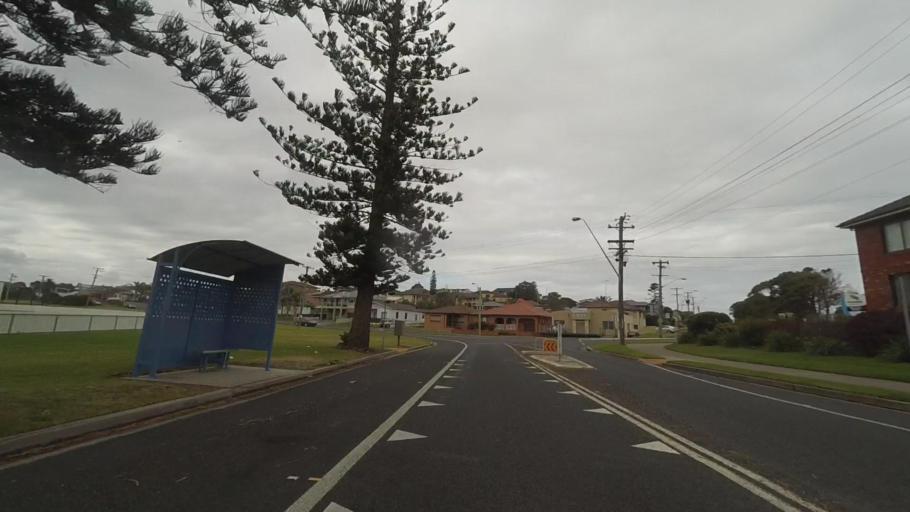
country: AU
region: New South Wales
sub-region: Wollongong
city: Port Kembla
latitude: -34.4897
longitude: 150.9114
